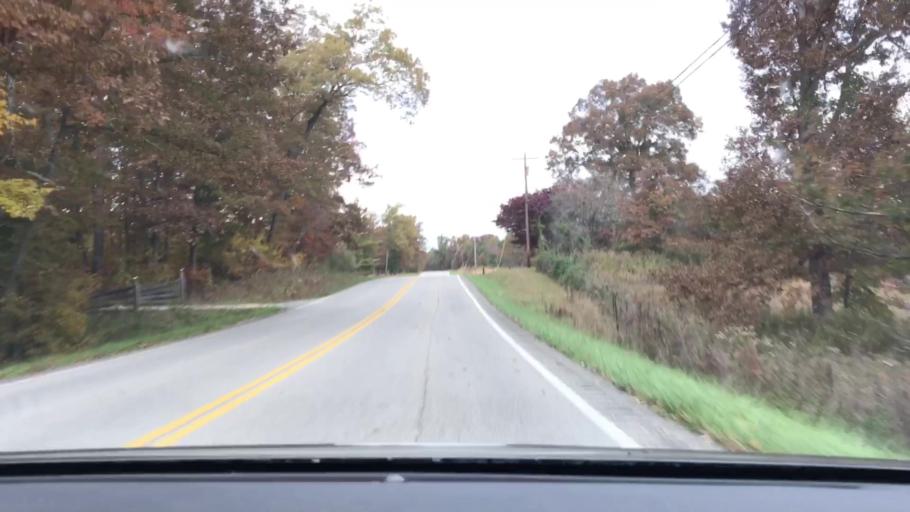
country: US
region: Tennessee
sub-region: Scott County
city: Huntsville
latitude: 36.3441
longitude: -84.6526
